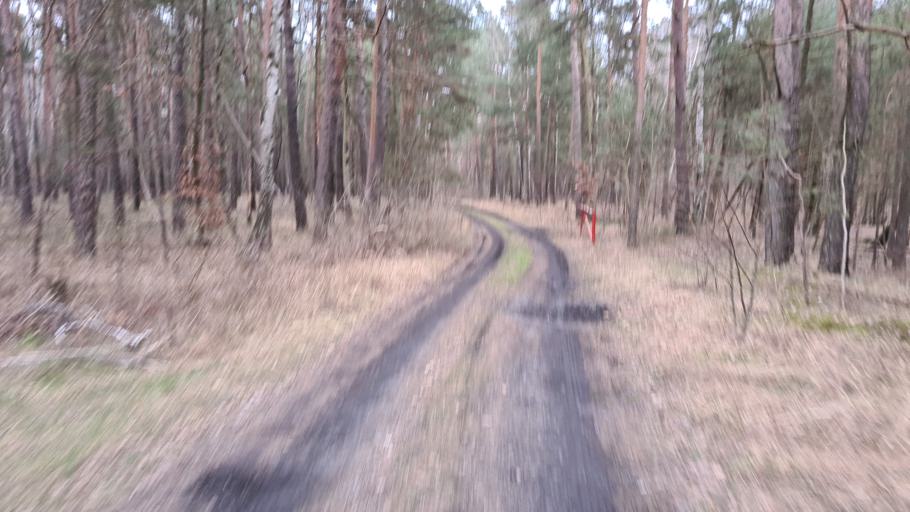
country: DE
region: Brandenburg
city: Trobitz
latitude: 51.5994
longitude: 13.4559
